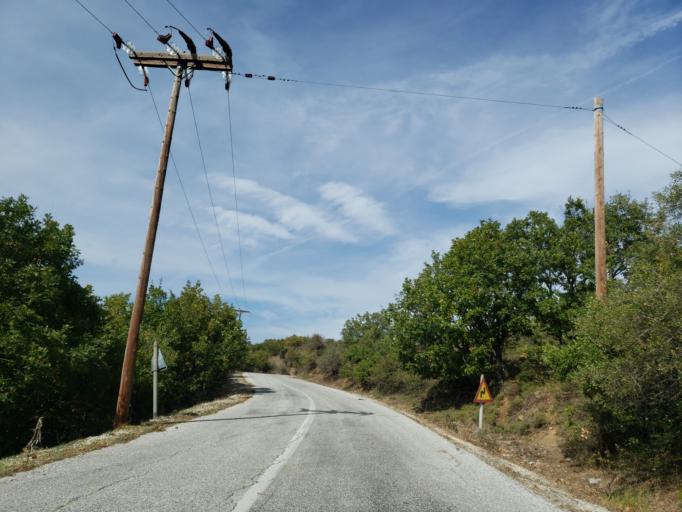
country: GR
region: Thessaly
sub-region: Trikala
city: Kastraki
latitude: 39.7333
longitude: 21.6552
